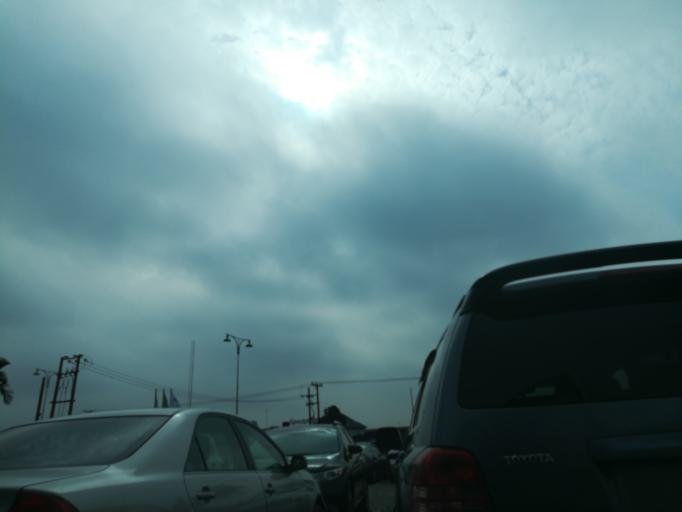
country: NG
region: Rivers
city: Port Harcourt
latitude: 4.8159
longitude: 7.0052
